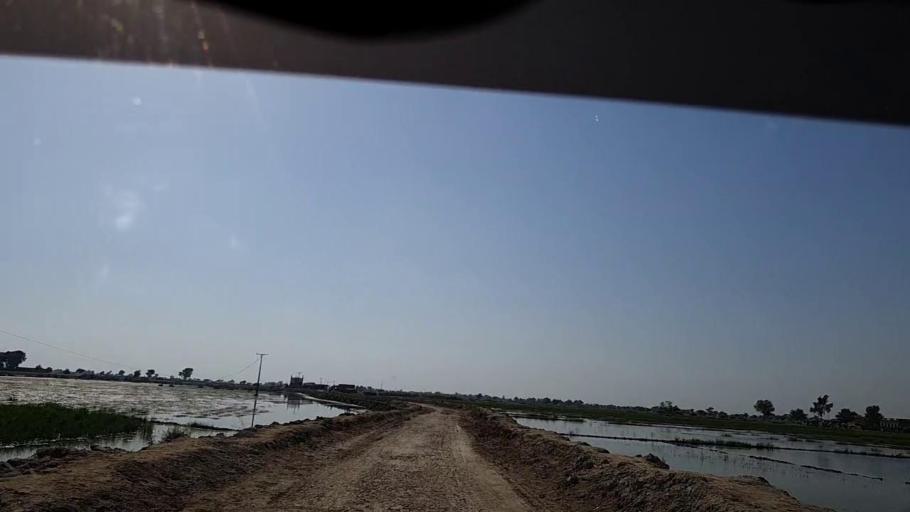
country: PK
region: Sindh
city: Tangwani
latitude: 28.3621
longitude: 69.0170
